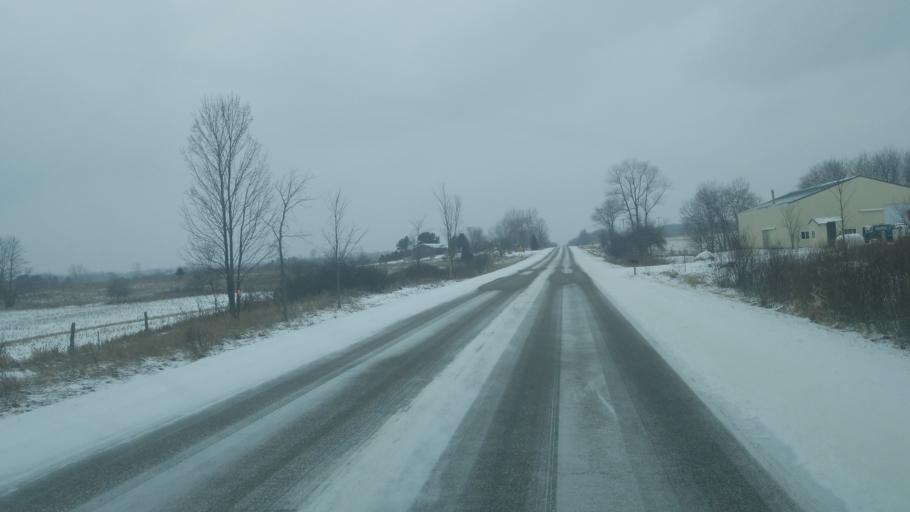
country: US
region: Michigan
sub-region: Osceola County
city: Evart
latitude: 44.1025
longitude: -85.1809
